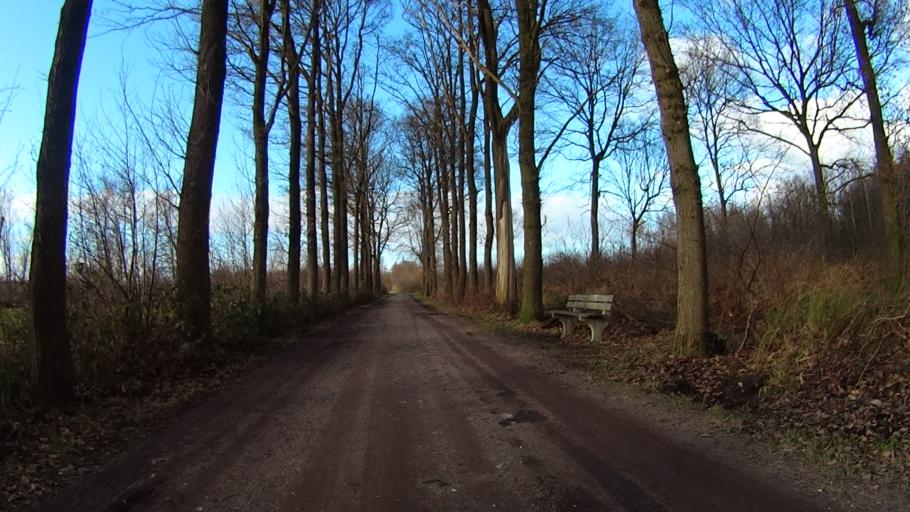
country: NL
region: Gelderland
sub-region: Gemeente Barneveld
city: Terschuur
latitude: 52.1699
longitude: 5.5220
